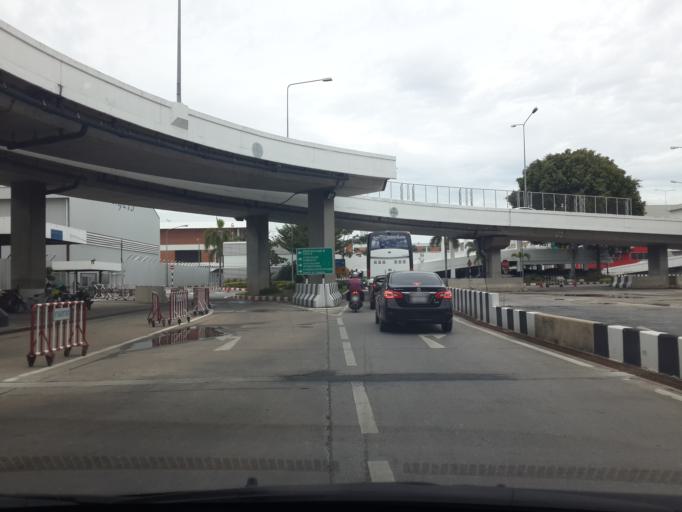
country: TH
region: Bangkok
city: Don Mueang
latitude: 13.9258
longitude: 100.6059
